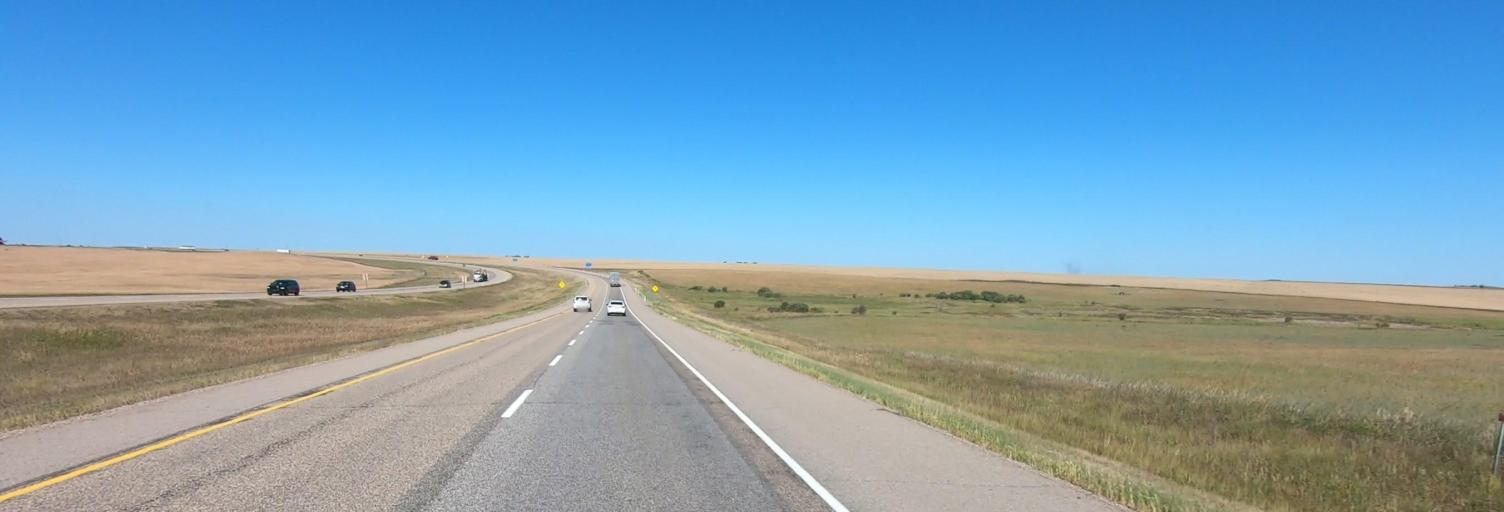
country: CA
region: Alberta
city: Bassano
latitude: 50.8590
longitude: -112.8489
